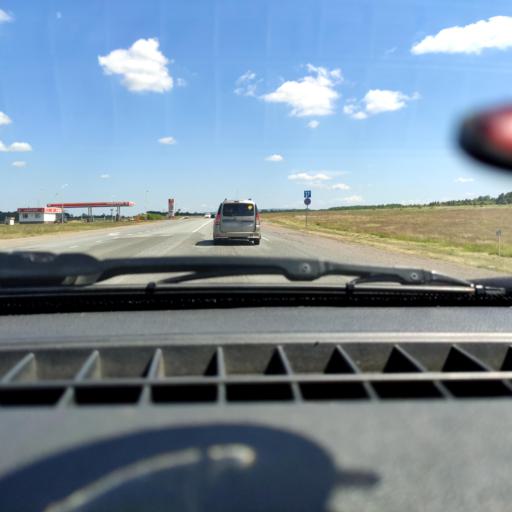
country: RU
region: Bashkortostan
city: Kudeyevskiy
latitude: 54.8172
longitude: 56.8022
